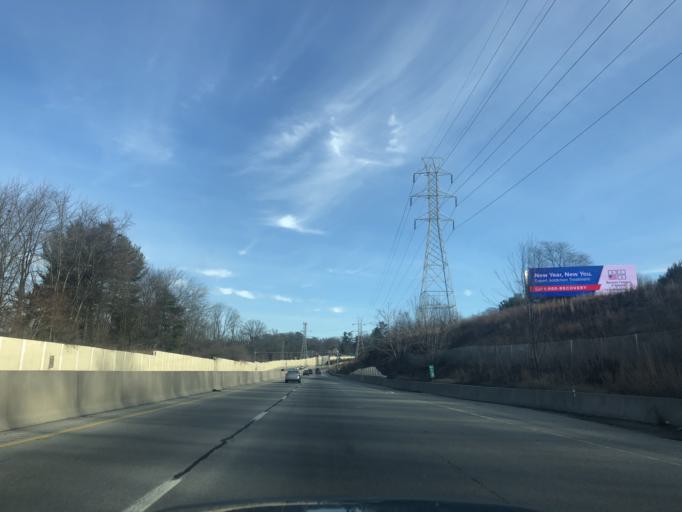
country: US
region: Pennsylvania
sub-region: Montgomery County
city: Wyndmoor
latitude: 40.1001
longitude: -75.1872
